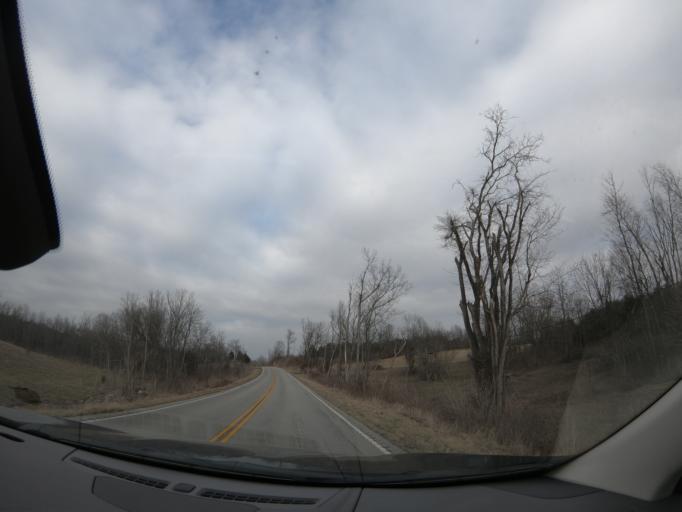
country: US
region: Kentucky
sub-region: Spencer County
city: Taylorsville
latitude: 37.8782
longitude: -85.3053
